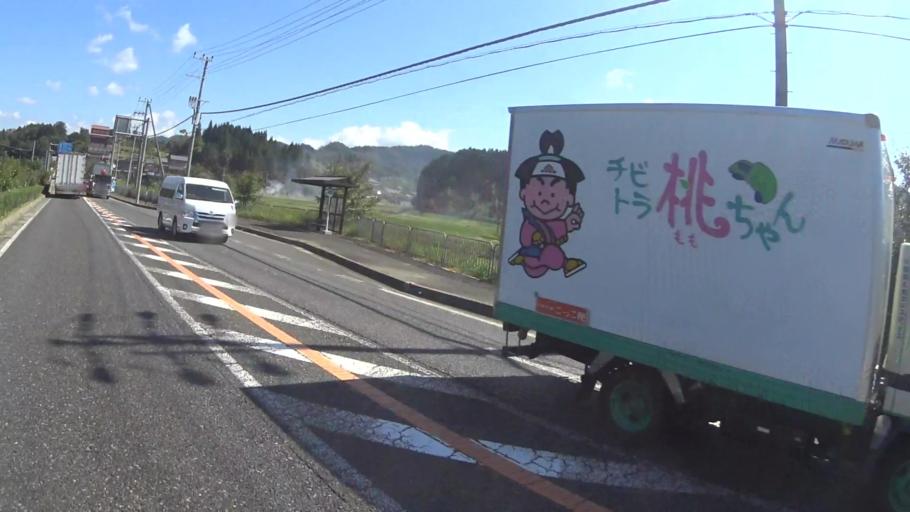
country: JP
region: Kyoto
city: Ayabe
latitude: 35.3387
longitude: 135.3081
